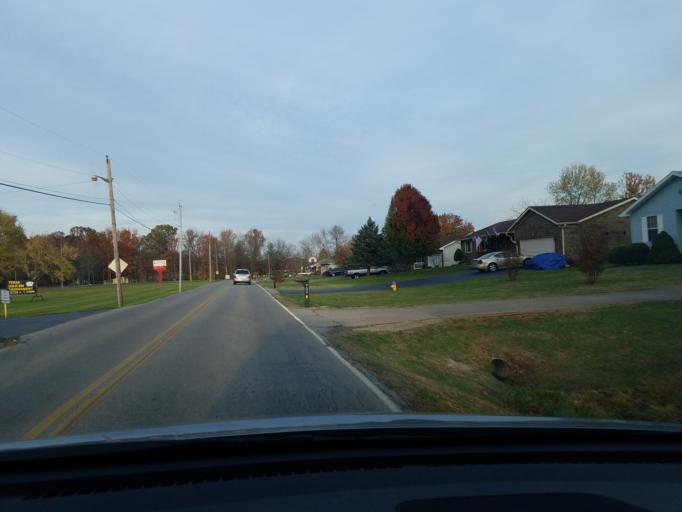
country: US
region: Indiana
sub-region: Clark County
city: Clarksville
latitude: 38.3313
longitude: -85.7793
